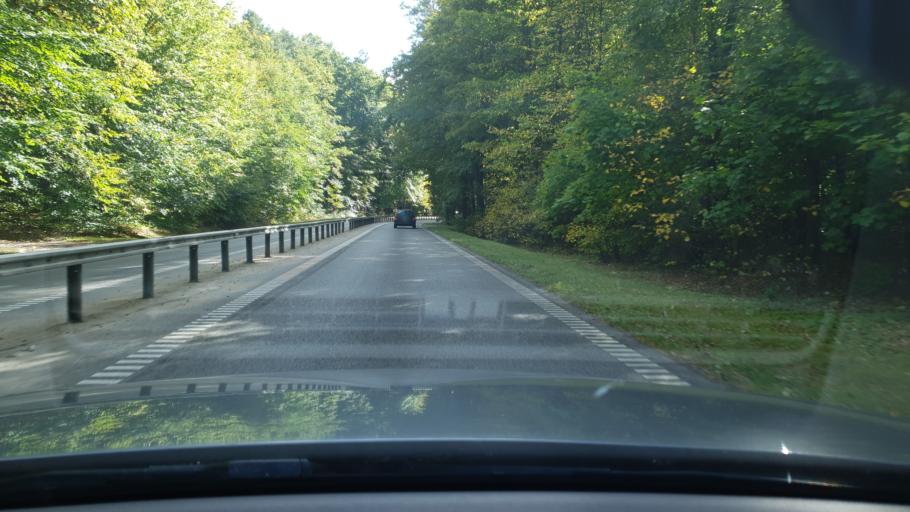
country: PL
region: Pomeranian Voivodeship
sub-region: Powiat wejherowski
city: Rekowo Dolne
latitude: 54.6309
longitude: 18.3442
